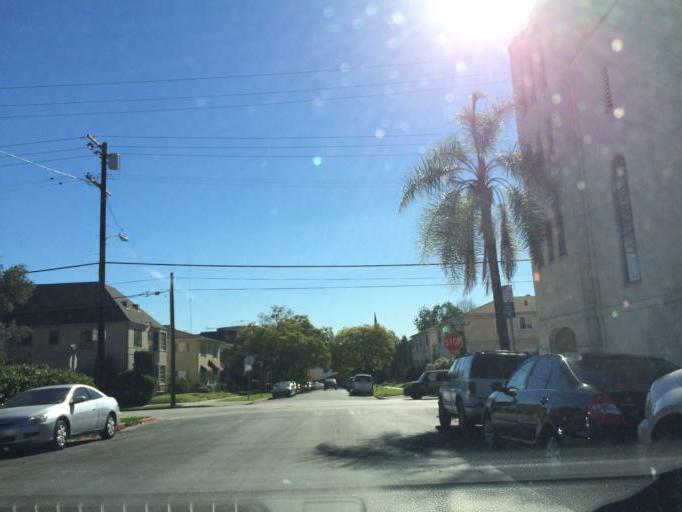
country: US
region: California
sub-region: Los Angeles County
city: Silver Lake
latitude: 34.1022
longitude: -118.2896
